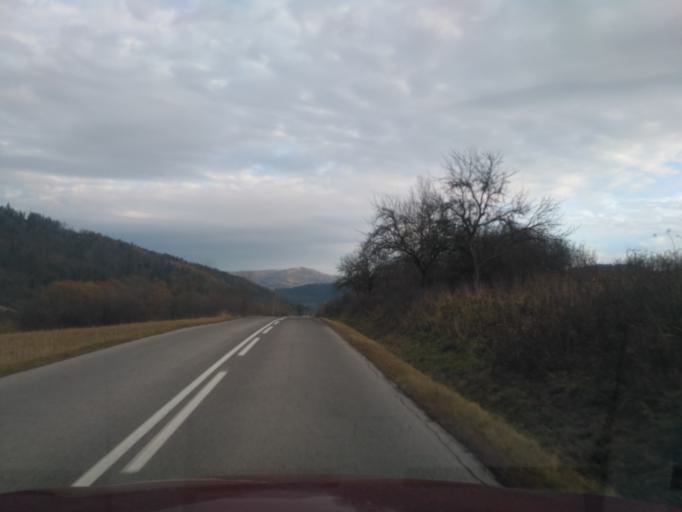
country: SK
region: Kosicky
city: Krompachy
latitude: 48.8016
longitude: 20.7324
